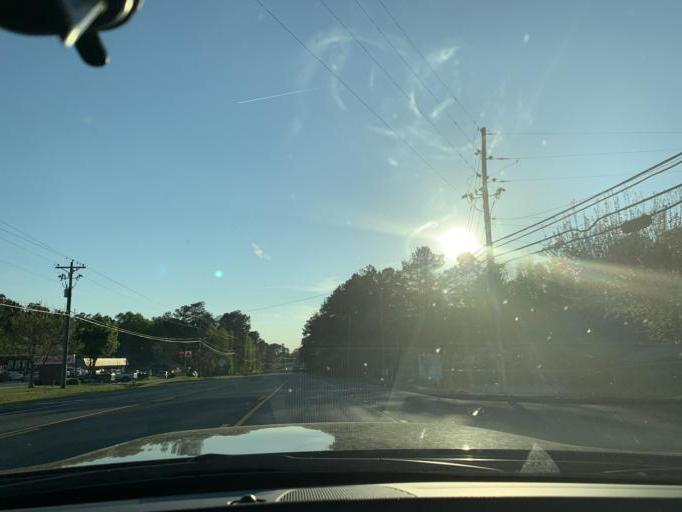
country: US
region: Georgia
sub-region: Forsyth County
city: Cumming
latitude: 34.2392
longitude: -84.1959
